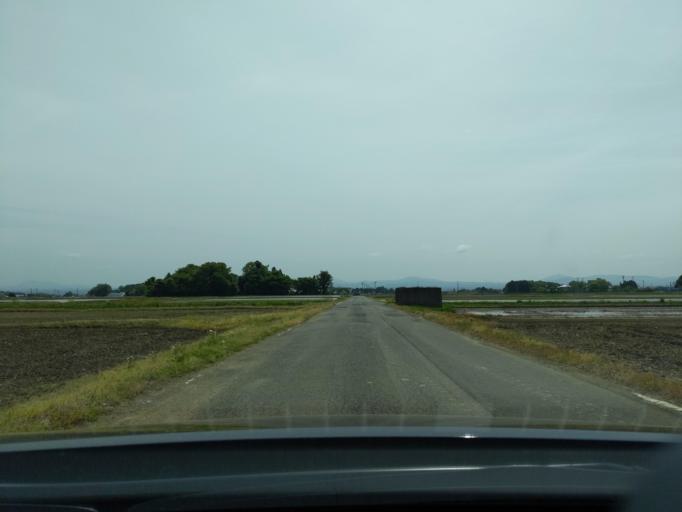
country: JP
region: Fukushima
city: Koriyama
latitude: 37.3975
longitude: 140.2838
